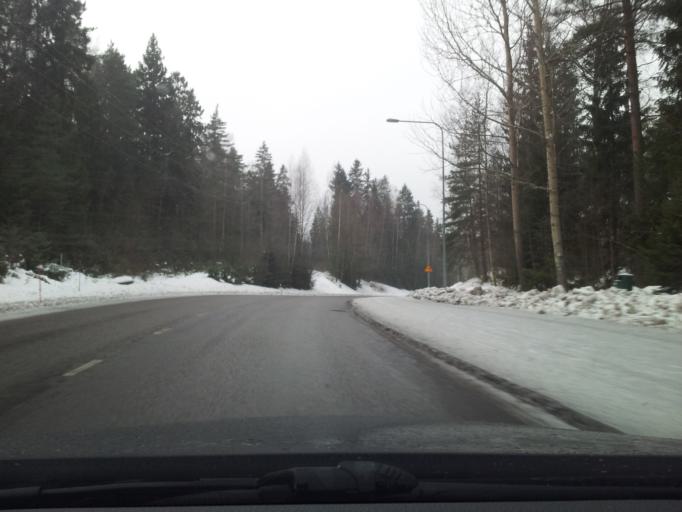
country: FI
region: Uusimaa
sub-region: Helsinki
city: Kauniainen
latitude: 60.1749
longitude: 24.7205
